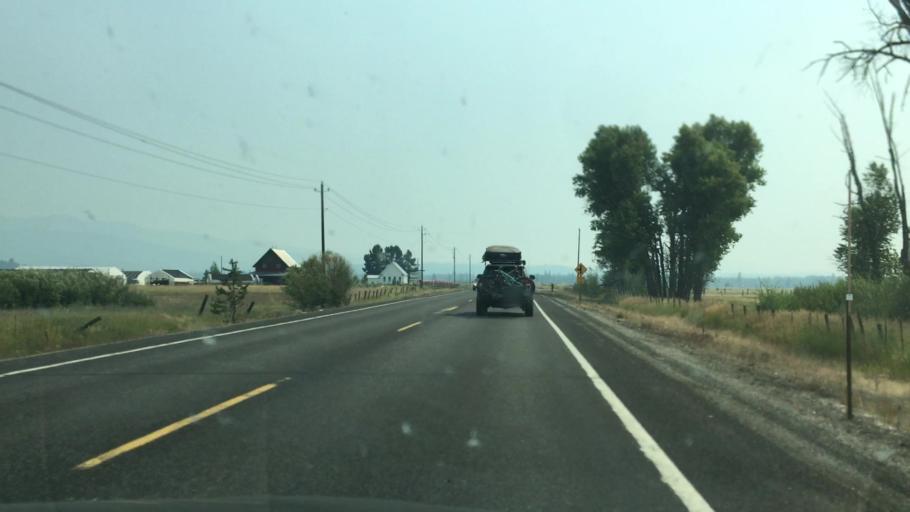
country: US
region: Idaho
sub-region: Valley County
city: Cascade
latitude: 44.4281
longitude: -115.9995
